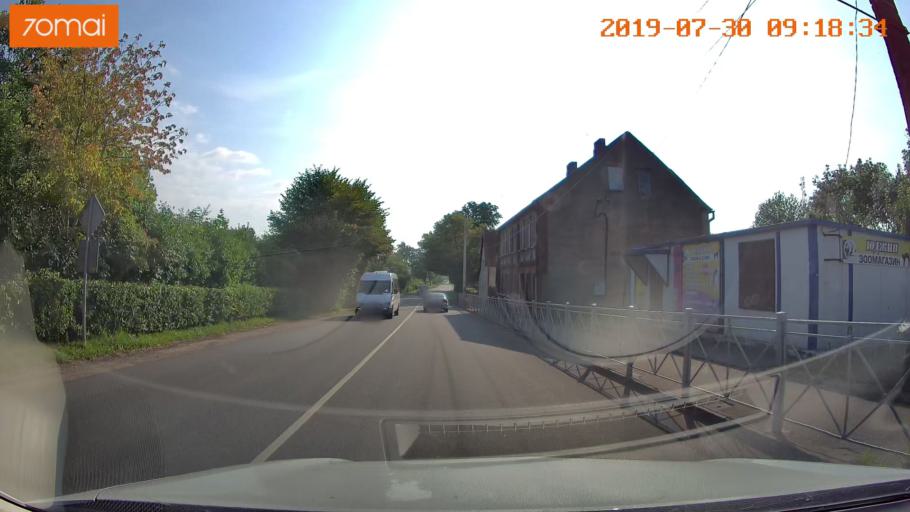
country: RU
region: Kaliningrad
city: Nesterov
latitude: 54.6306
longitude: 22.5775
